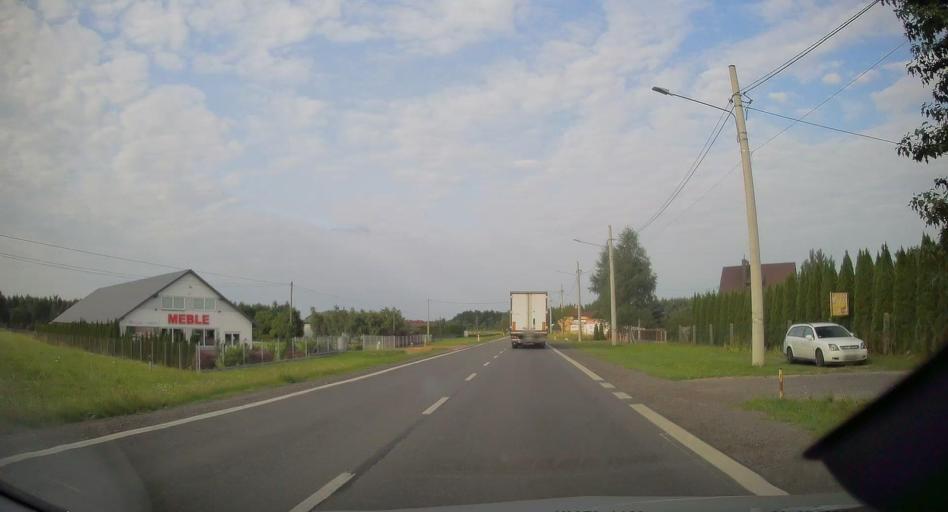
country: PL
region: Silesian Voivodeship
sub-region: Powiat czestochowski
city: Rudniki
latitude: 50.8853
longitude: 19.2585
